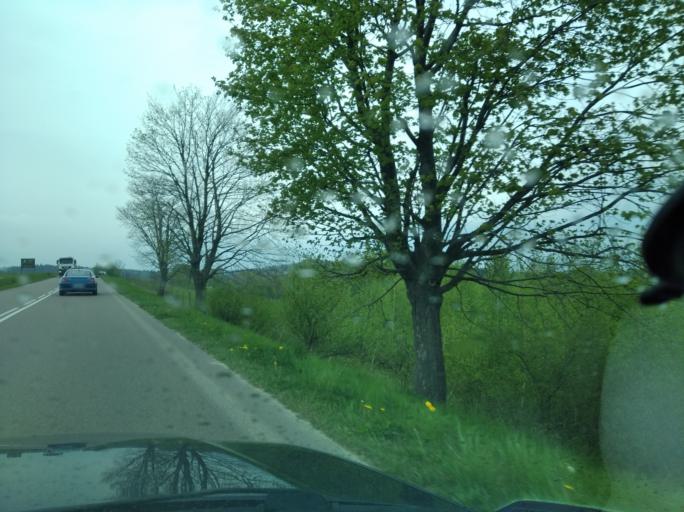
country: PL
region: Subcarpathian Voivodeship
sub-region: Powiat brzozowski
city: Wesola
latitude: 49.8321
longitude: 22.1570
